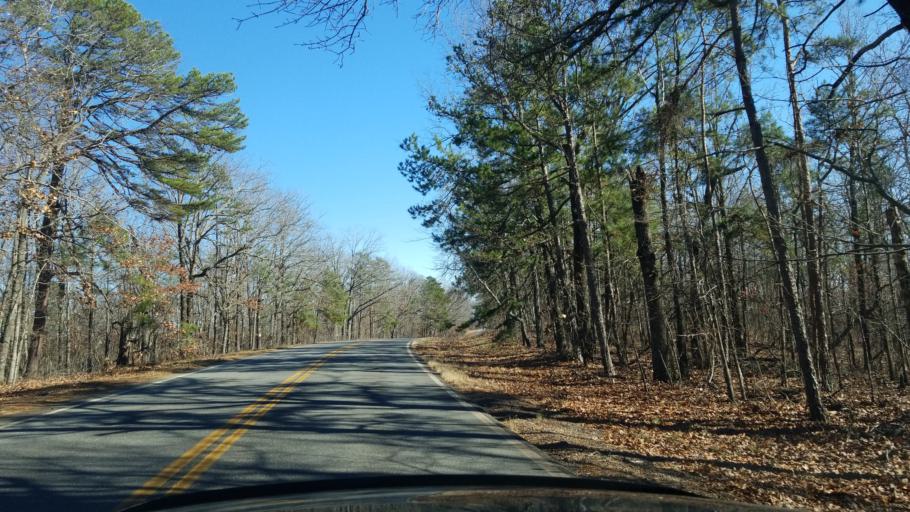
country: US
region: Georgia
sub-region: Talbot County
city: Sardis
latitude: 32.8437
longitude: -84.6880
